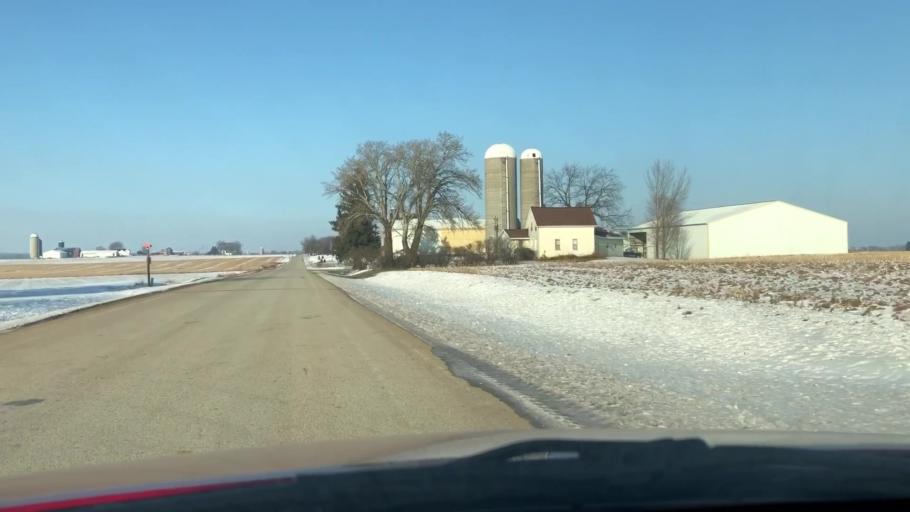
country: US
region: Wisconsin
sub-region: Outagamie County
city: Seymour
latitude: 44.4906
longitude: -88.3090
